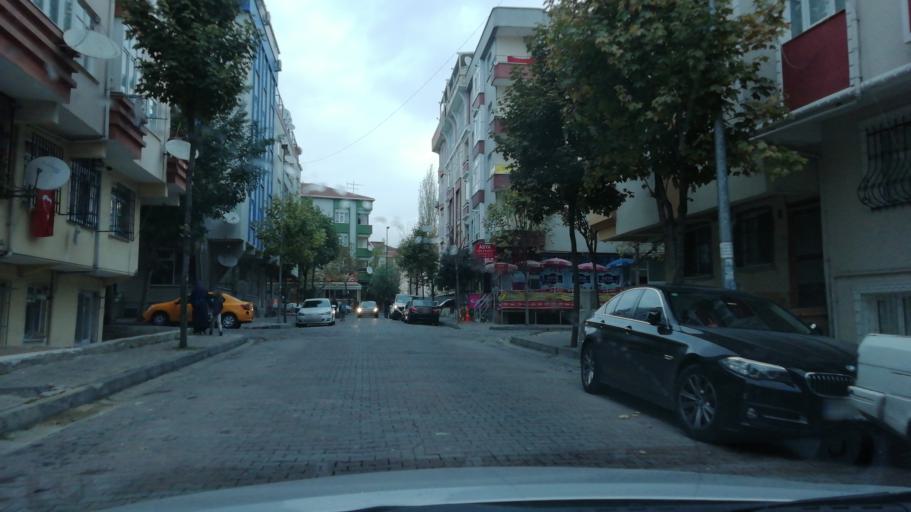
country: TR
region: Istanbul
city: Bahcelievler
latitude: 41.0174
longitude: 28.8333
